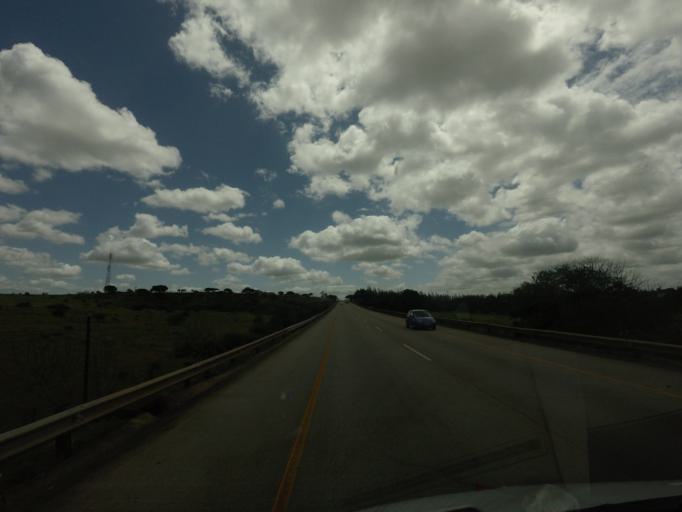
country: ZA
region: KwaZulu-Natal
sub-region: uMkhanyakude District Municipality
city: Mtubatuba
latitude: -28.4805
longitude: 32.1435
